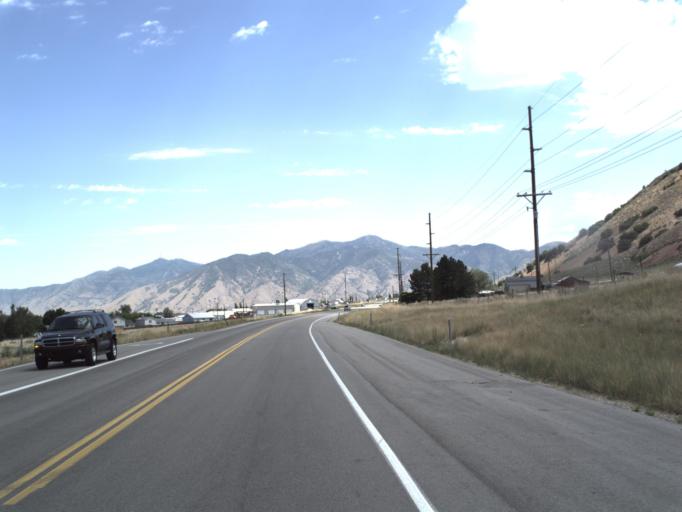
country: US
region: Utah
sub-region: Tooele County
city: Tooele
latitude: 40.5051
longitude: -112.3199
